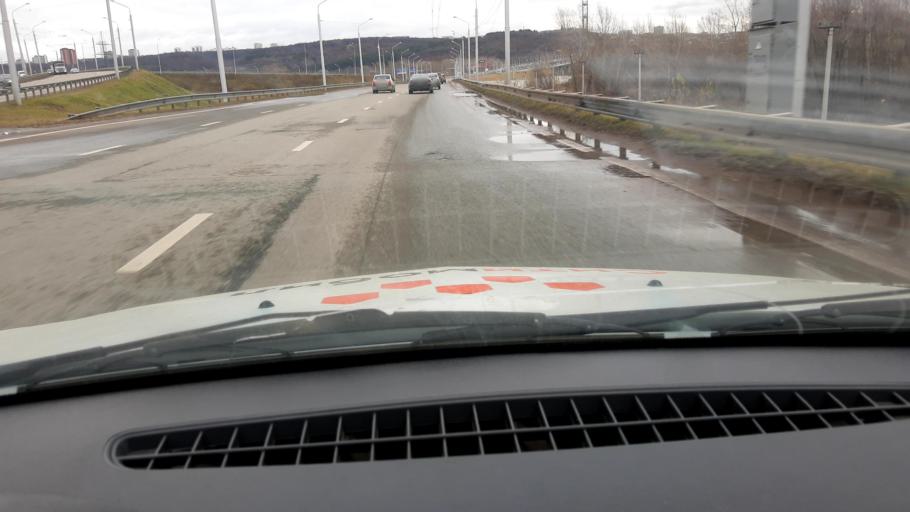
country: RU
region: Bashkortostan
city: Ufa
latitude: 54.7641
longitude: 55.9504
